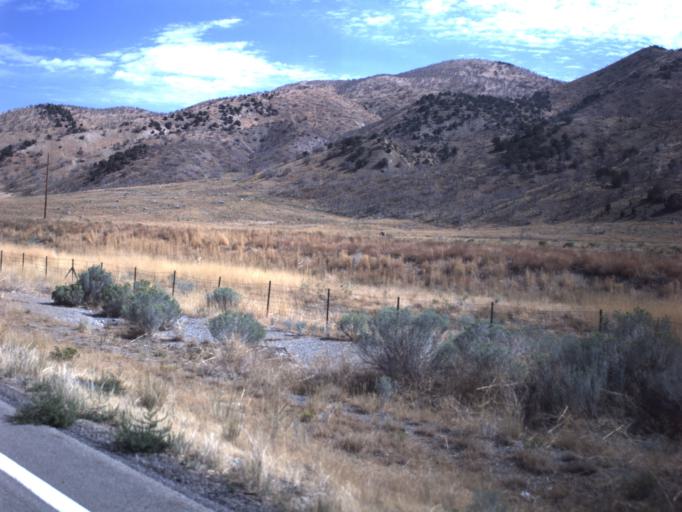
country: US
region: Utah
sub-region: Juab County
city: Nephi
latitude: 39.5137
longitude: -111.8683
